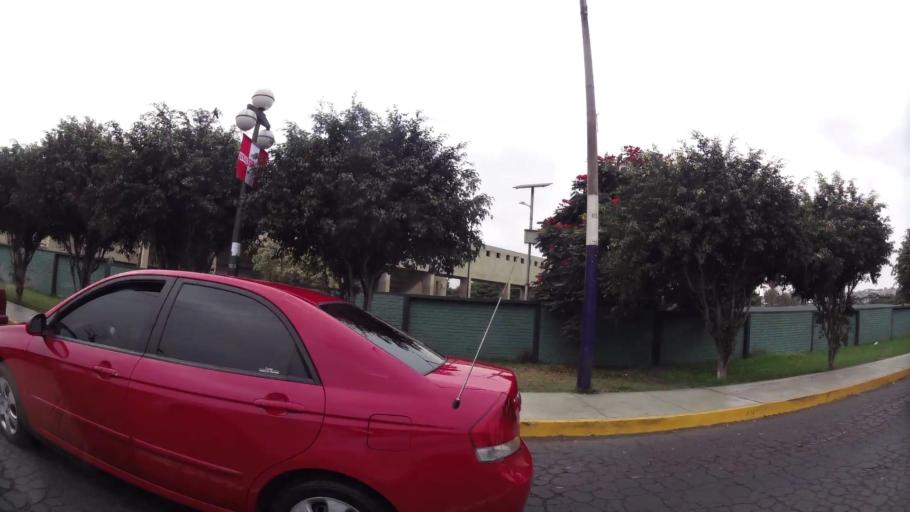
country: PE
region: Lima
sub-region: Lima
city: Surco
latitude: -12.1748
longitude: -76.9934
